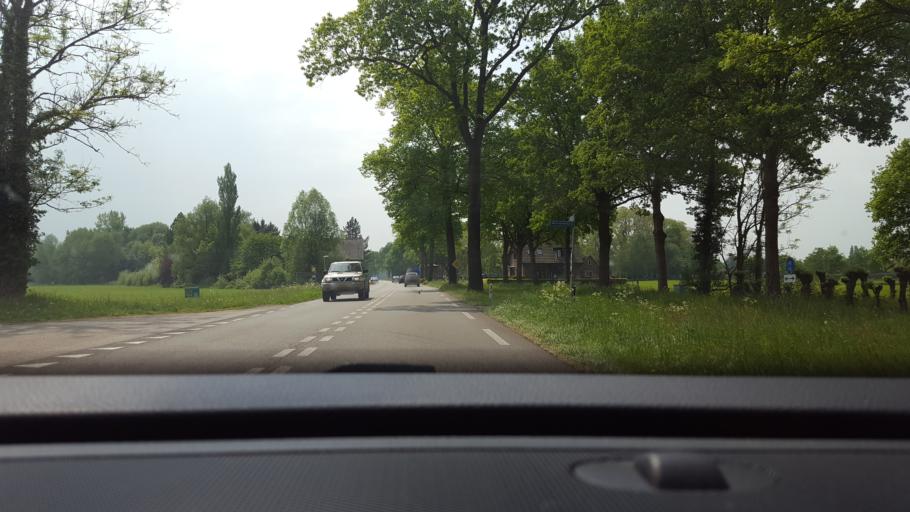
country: NL
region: Gelderland
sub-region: Gemeente Bronckhorst
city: Hengelo
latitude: 52.0713
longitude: 6.3118
